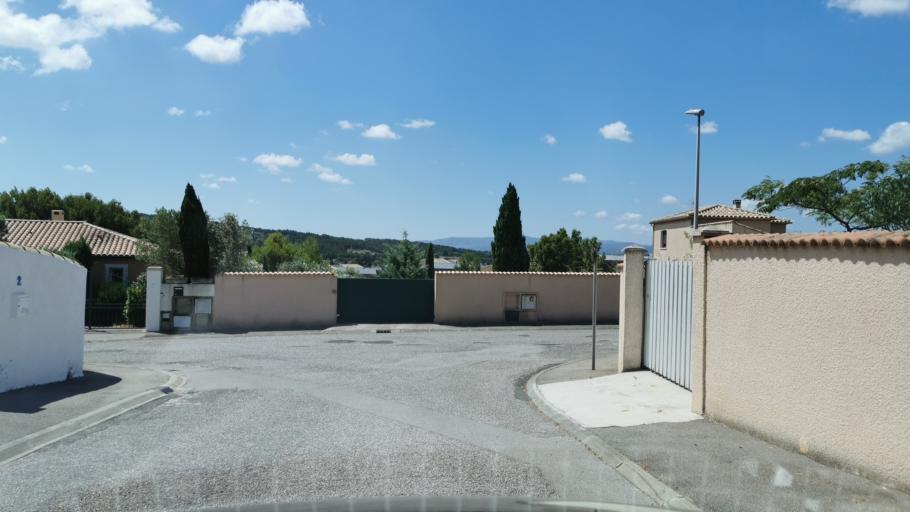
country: FR
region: Languedoc-Roussillon
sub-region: Departement de l'Aude
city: Peyriac-de-Mer
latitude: 43.1383
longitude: 2.9649
